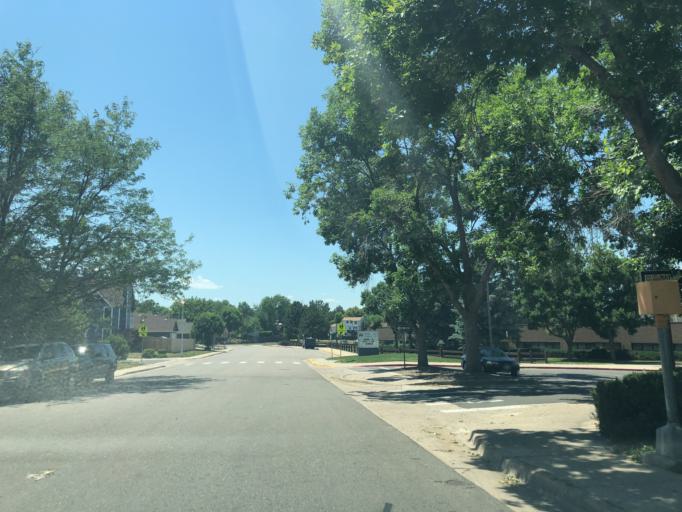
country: US
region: Colorado
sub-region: Arapahoe County
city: Dove Valley
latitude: 39.6260
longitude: -104.7783
